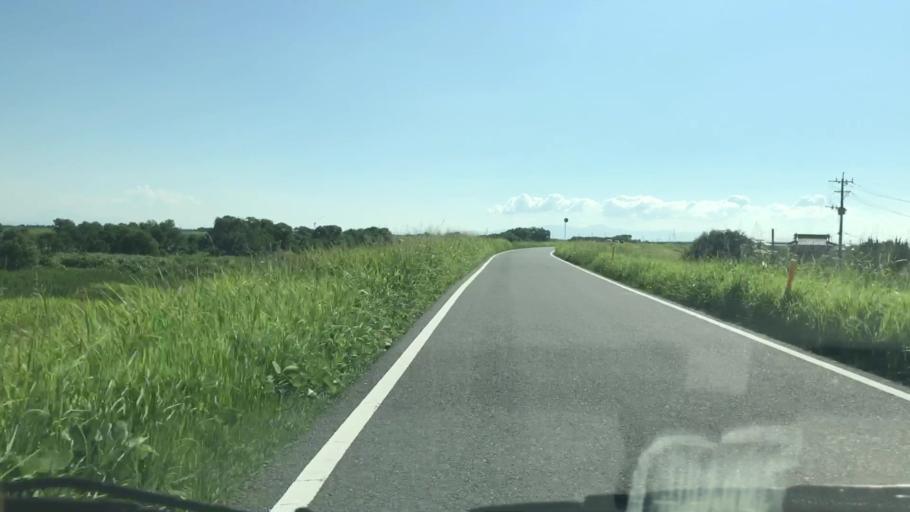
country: JP
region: Saga Prefecture
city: Kanzakimachi-kanzaki
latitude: 33.2779
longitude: 130.4458
